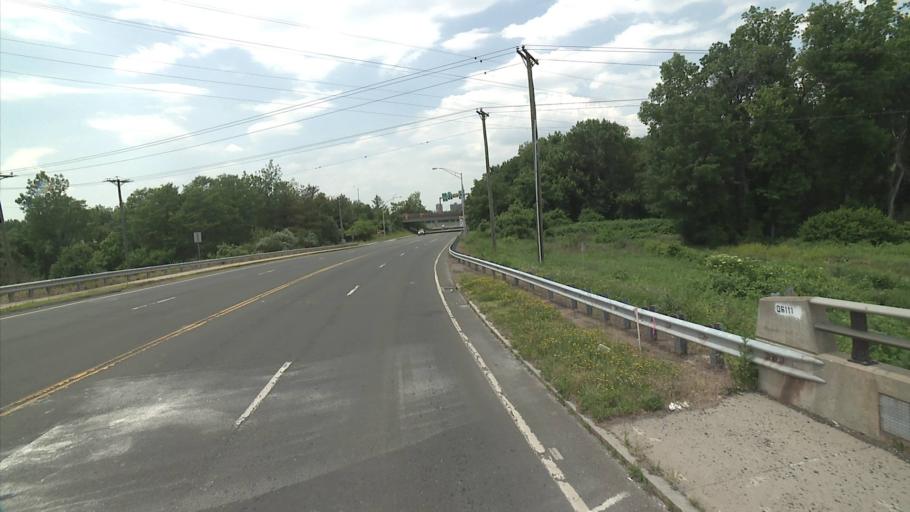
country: US
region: Connecticut
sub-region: Hartford County
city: Hartford
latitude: 41.7587
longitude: -72.6505
